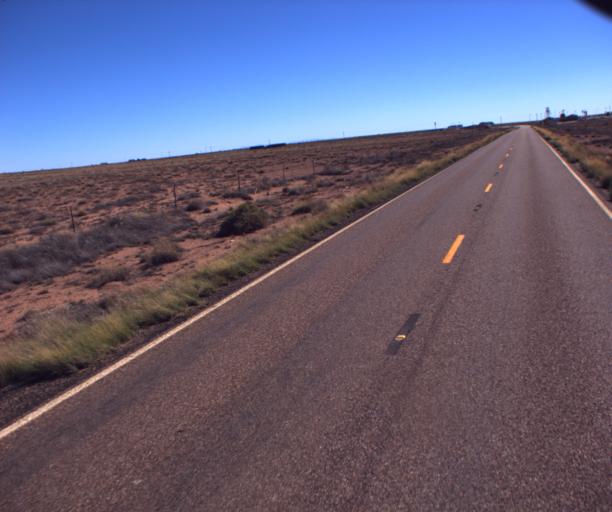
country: US
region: Arizona
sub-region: Navajo County
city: Holbrook
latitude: 34.9816
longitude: -110.0887
